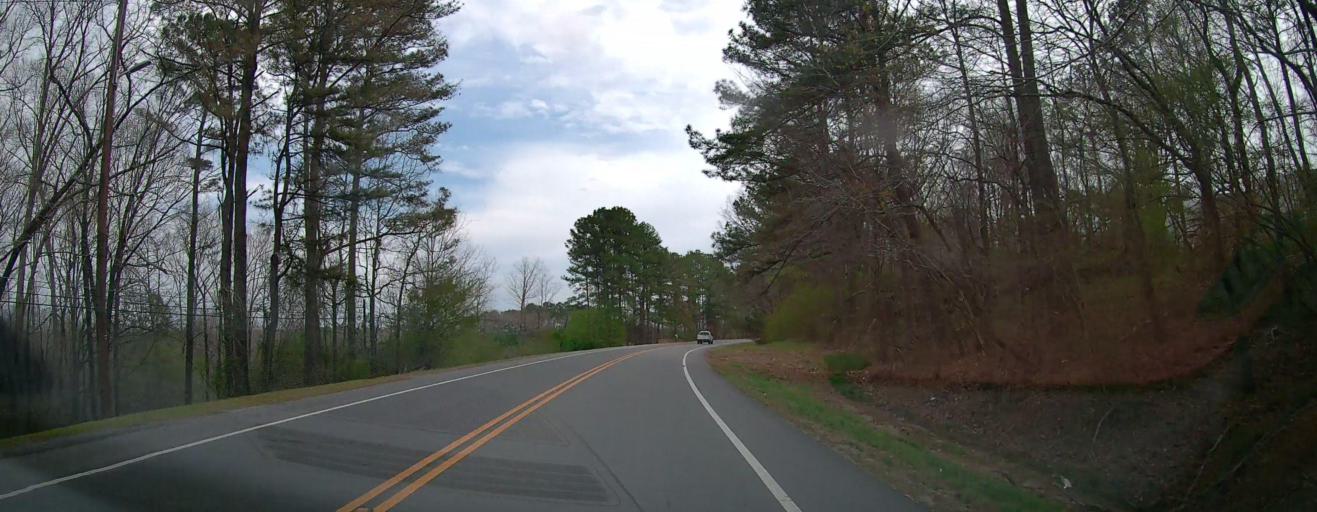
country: US
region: Alabama
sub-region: Marion County
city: Guin
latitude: 33.9853
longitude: -87.9195
